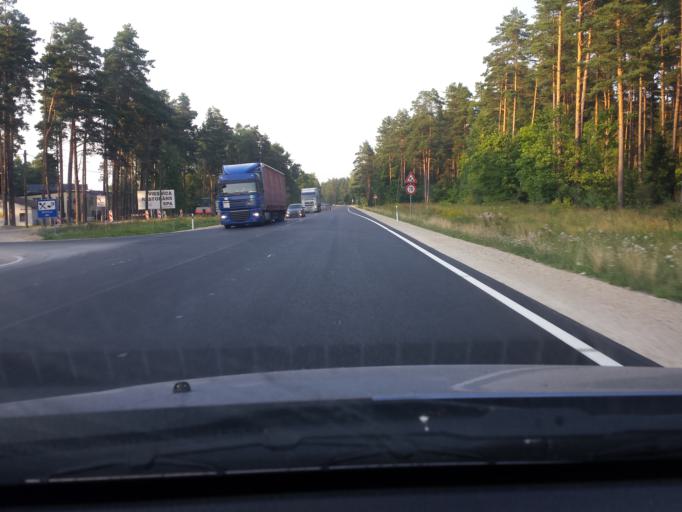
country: LV
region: Riga
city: Bergi
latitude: 57.0207
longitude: 24.3145
